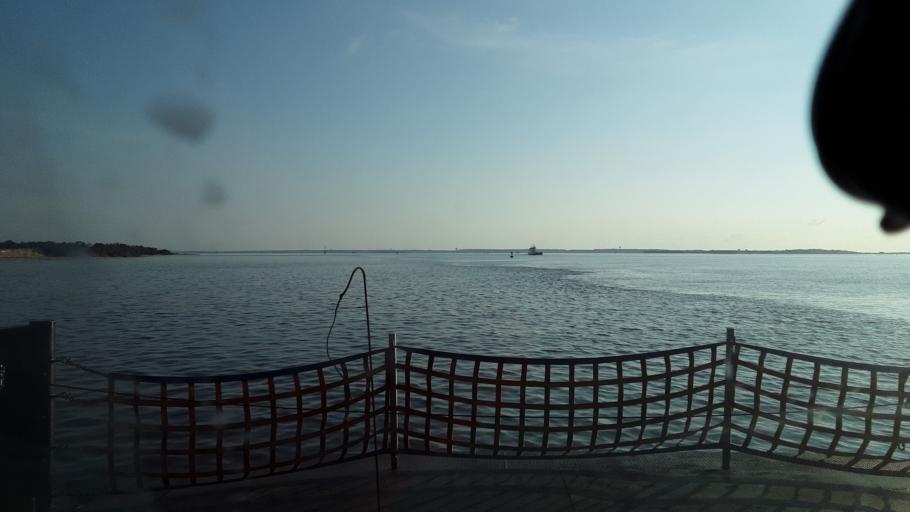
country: US
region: North Carolina
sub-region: Brunswick County
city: Southport
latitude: 33.9515
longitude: -77.9634
